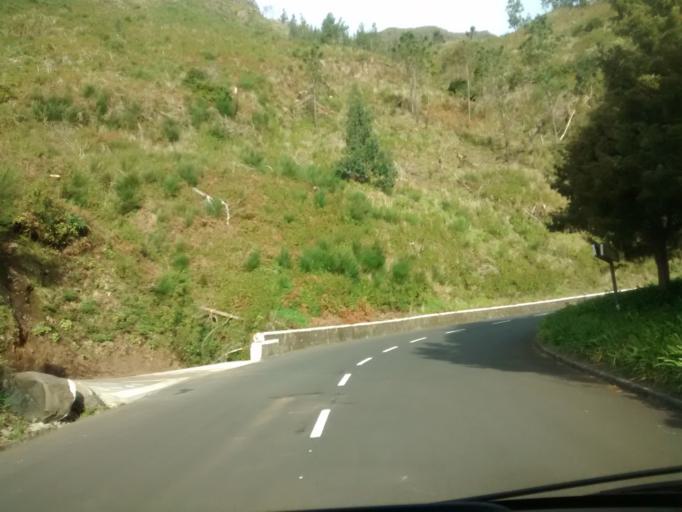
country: PT
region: Madeira
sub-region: Sao Vicente
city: Sao Vicente
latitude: 32.7432
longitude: -17.0251
